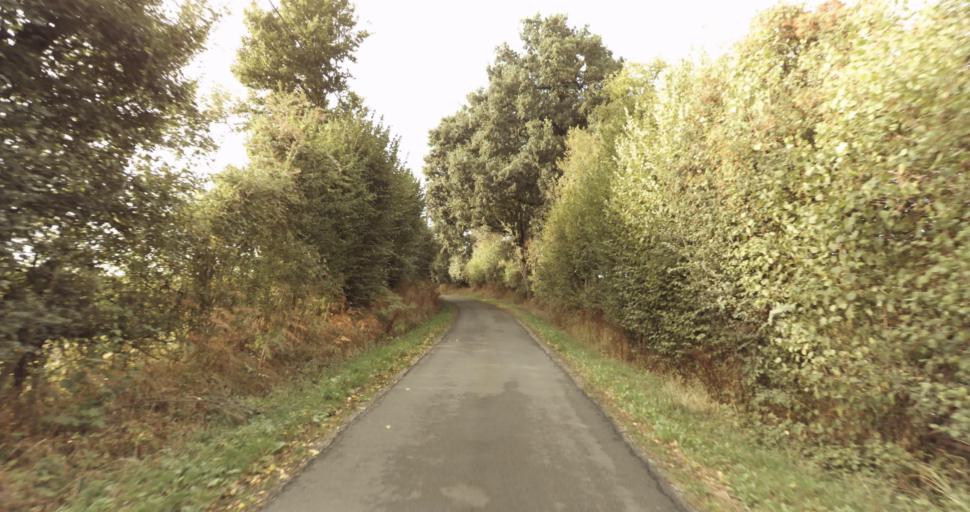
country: FR
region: Lower Normandy
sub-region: Departement de l'Orne
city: Sees
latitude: 48.6896
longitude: 0.2459
